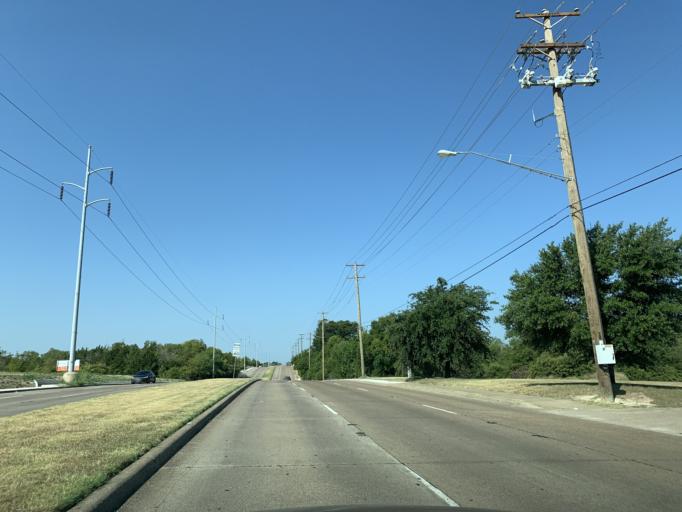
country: US
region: Texas
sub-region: Dallas County
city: Hutchins
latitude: 32.6724
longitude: -96.7636
